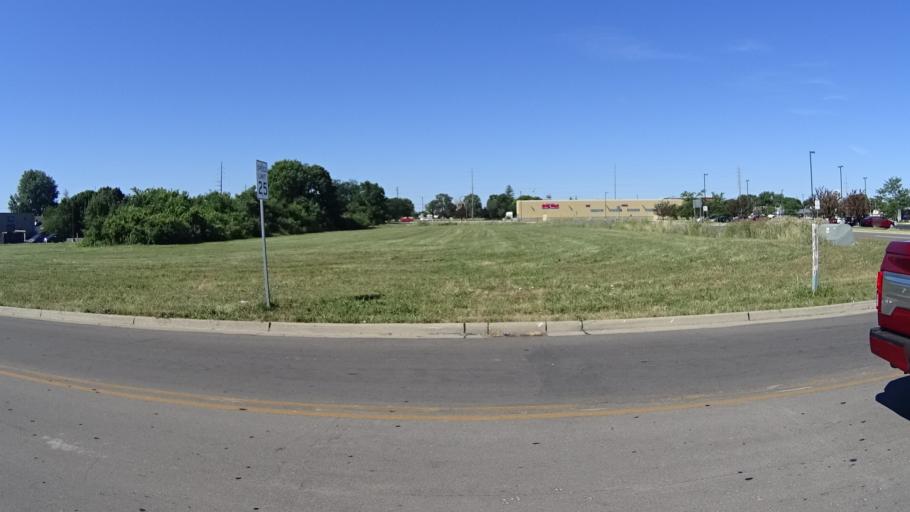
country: US
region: Ohio
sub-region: Erie County
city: Sandusky
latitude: 41.4240
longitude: -82.6761
